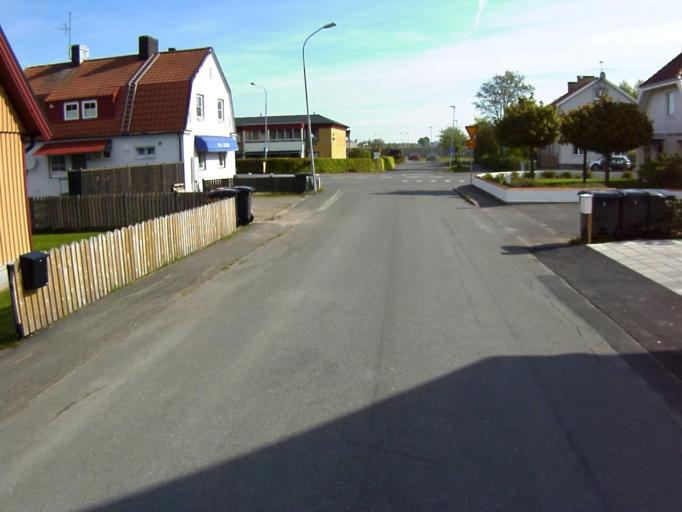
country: SE
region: Skane
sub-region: Kristianstads Kommun
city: Fjalkinge
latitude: 56.0422
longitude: 14.2804
